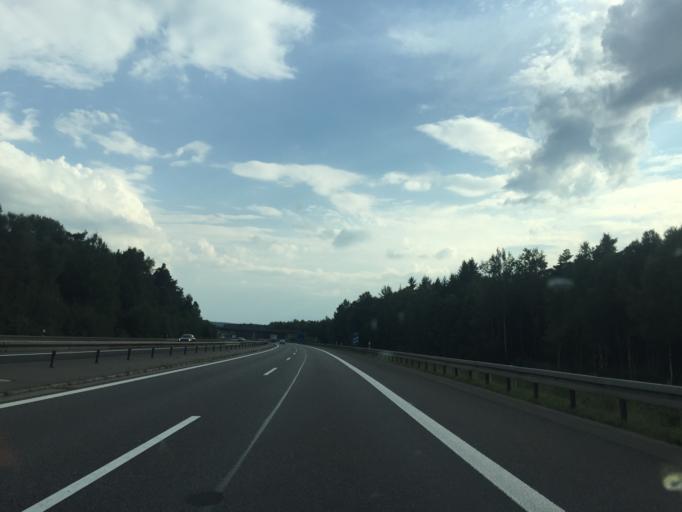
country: DE
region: Bavaria
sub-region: Upper Palatinate
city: Weiden
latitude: 49.7049
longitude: 12.1375
